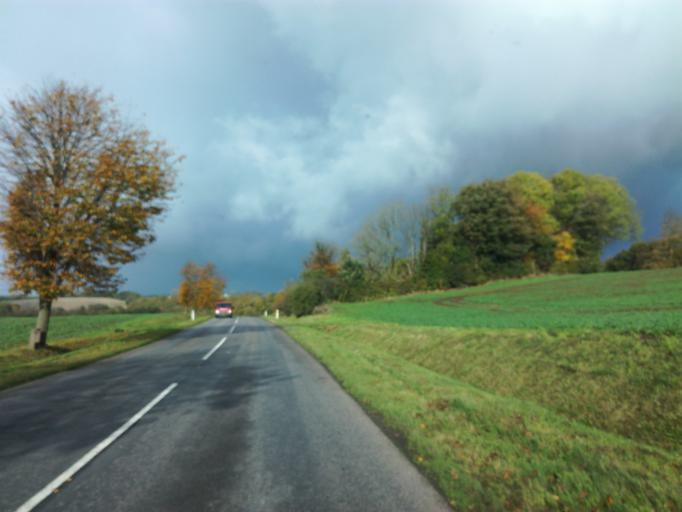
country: DK
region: South Denmark
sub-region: Vejle Kommune
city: Borkop
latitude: 55.6519
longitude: 9.6412
